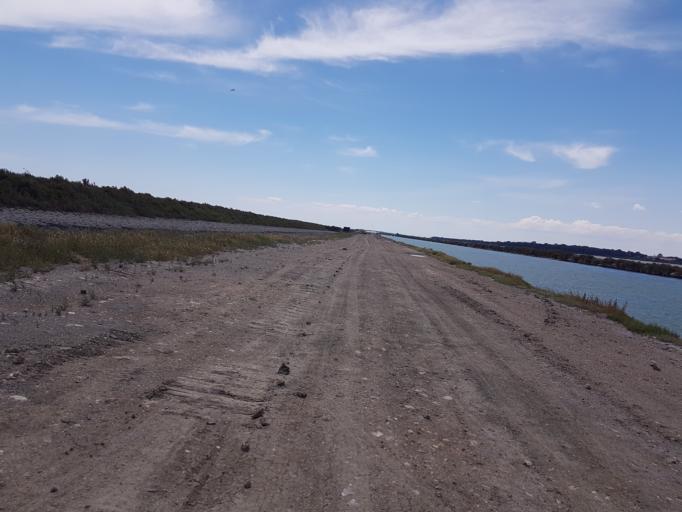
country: FR
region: Languedoc-Roussillon
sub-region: Departement de l'Herault
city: Vic-la-Gardiole
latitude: 43.4766
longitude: 3.8311
